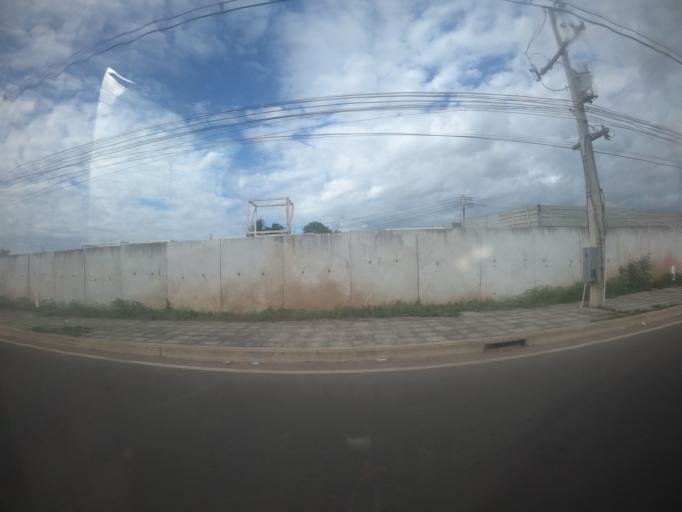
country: TH
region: Surin
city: Prasat
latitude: 14.6206
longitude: 103.4131
